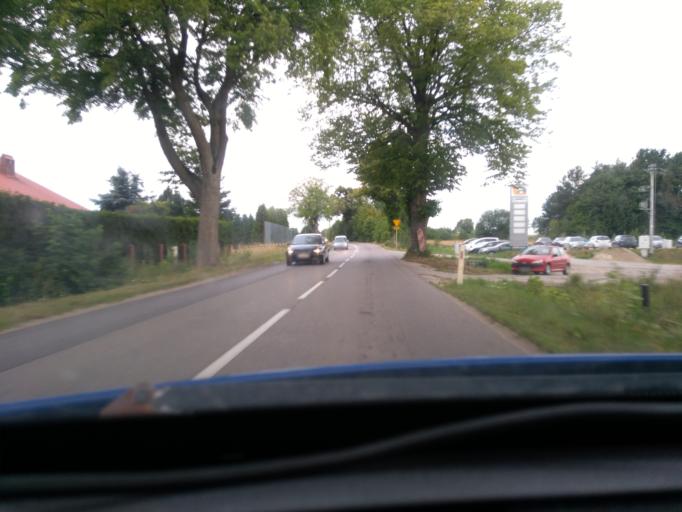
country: PL
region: Pomeranian Voivodeship
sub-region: Powiat kartuski
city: Zukowo
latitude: 54.3793
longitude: 18.3666
